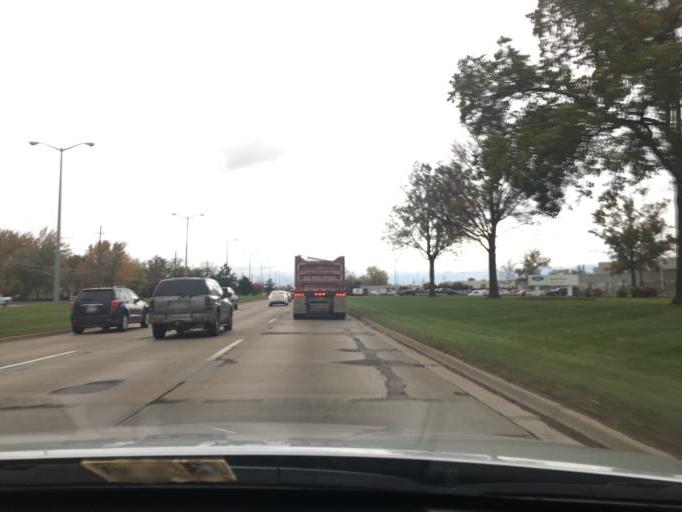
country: US
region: Michigan
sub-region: Macomb County
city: Sterling Heights
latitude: 42.5833
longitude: -83.0498
